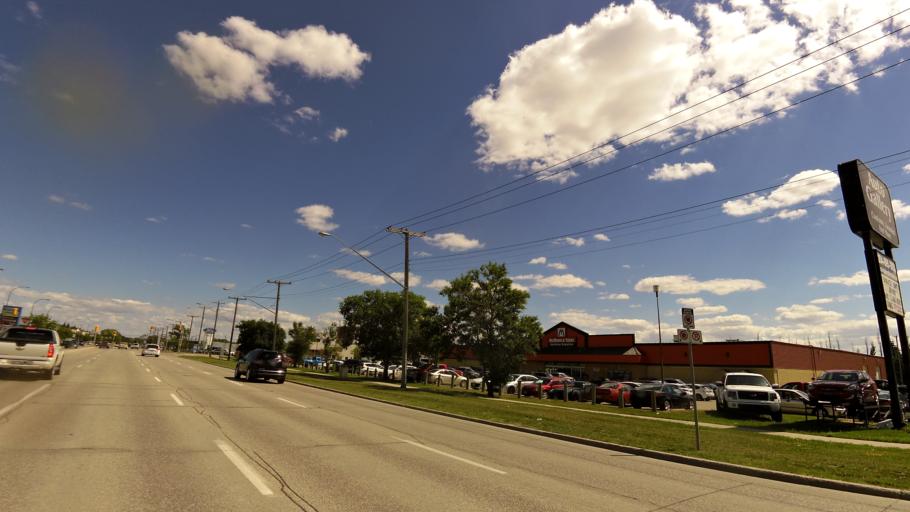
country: CA
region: Manitoba
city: Headingley
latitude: 49.8818
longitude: -97.3146
